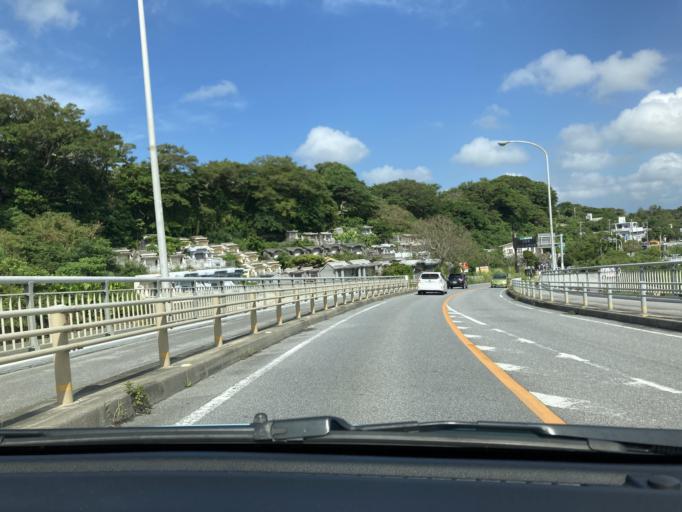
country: JP
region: Okinawa
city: Chatan
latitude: 26.2900
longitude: 127.7852
